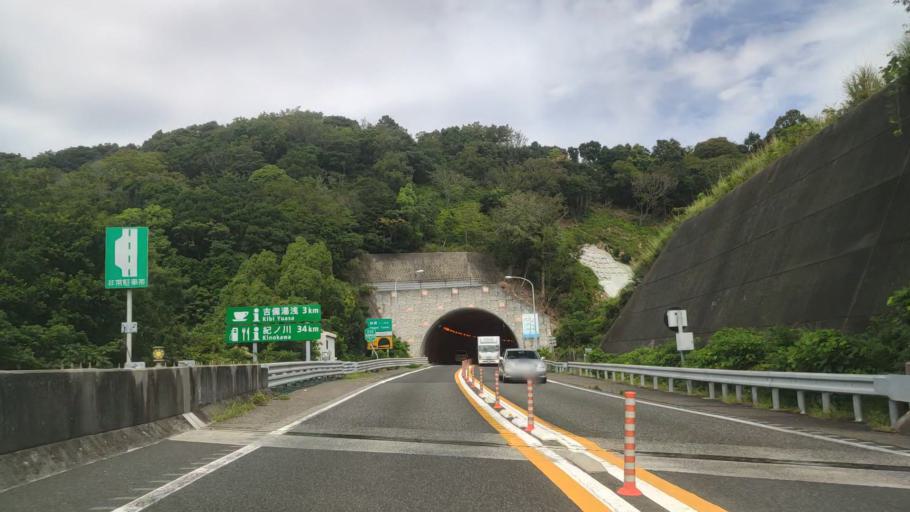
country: JP
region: Wakayama
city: Kainan
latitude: 34.0144
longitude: 135.1900
